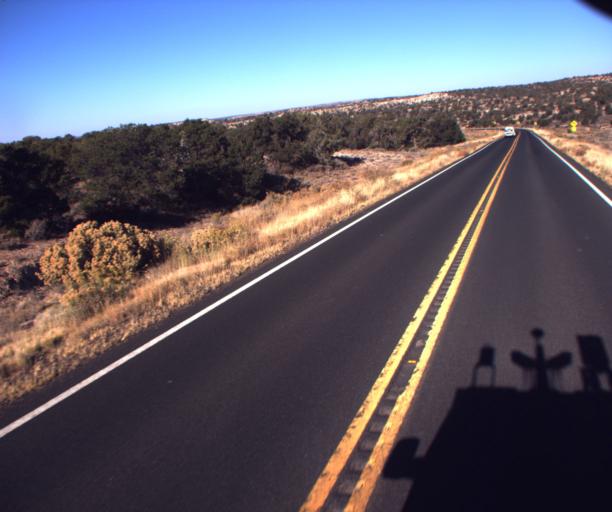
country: US
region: Arizona
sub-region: Apache County
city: Ganado
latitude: 35.7664
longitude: -109.7911
